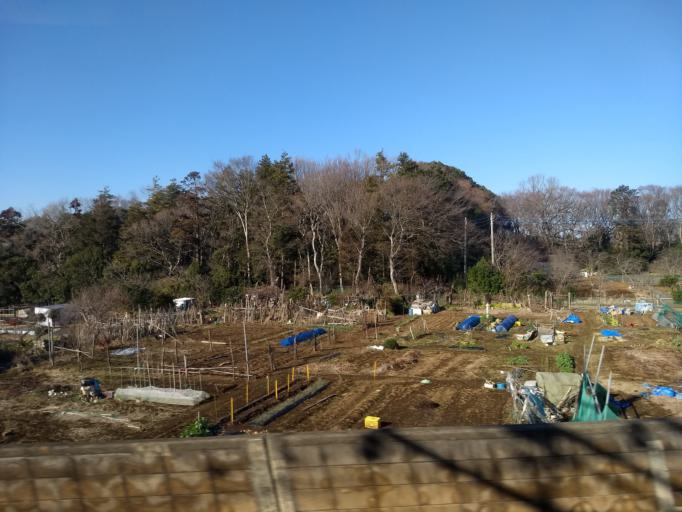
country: JP
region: Chiba
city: Shiroi
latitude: 35.7825
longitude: 140.0096
